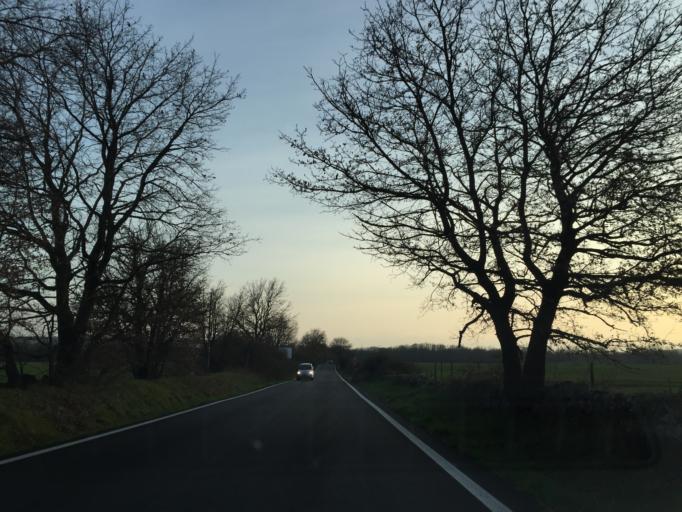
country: IT
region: Latium
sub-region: Citta metropolitana di Roma Capitale
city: Campagnano di Roma
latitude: 42.1762
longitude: 12.3596
